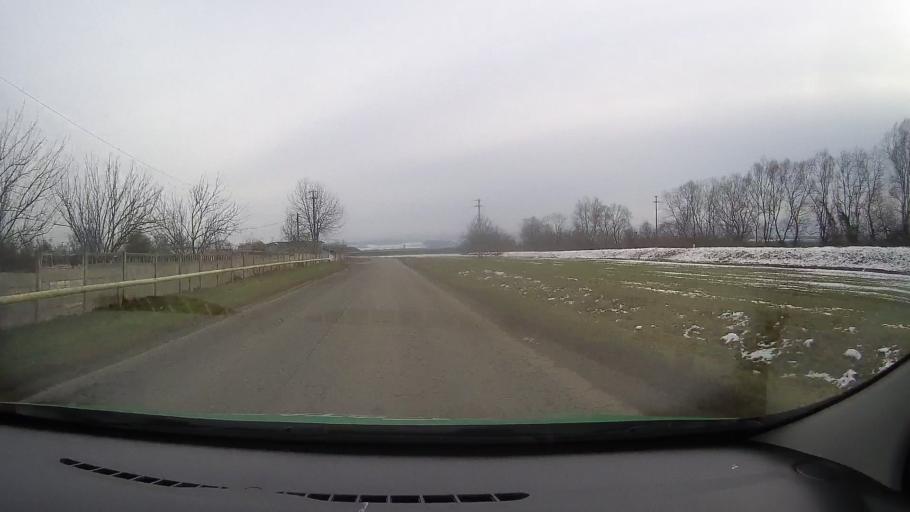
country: RO
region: Hunedoara
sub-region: Comuna Geoagiu
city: Geoagiu
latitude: 45.8892
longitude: 23.2354
